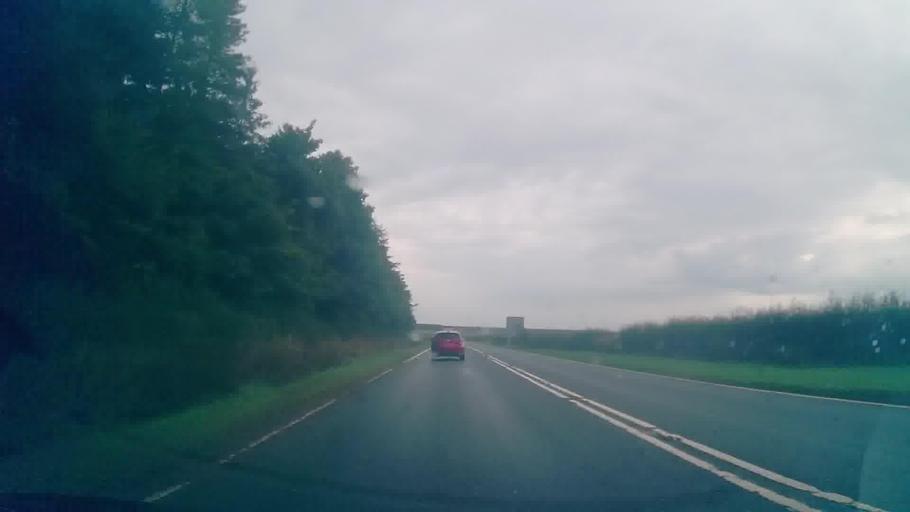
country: GB
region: Scotland
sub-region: Dumfries and Galloway
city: Annan
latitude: 55.0073
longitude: -3.3323
